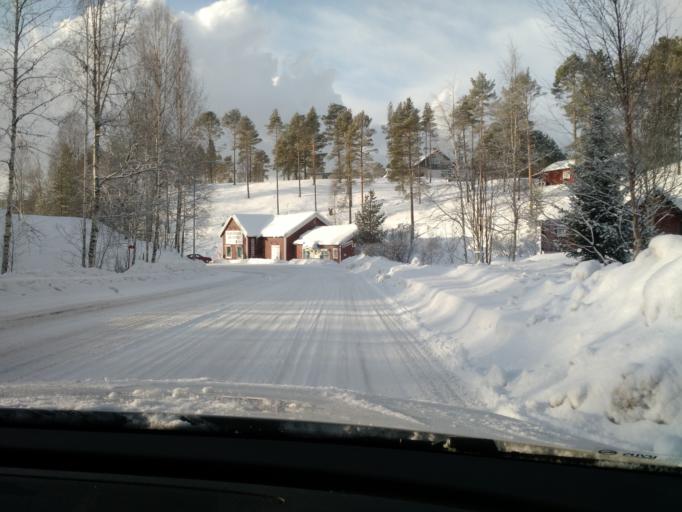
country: NO
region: Hedmark
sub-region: Trysil
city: Innbygda
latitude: 61.8600
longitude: 12.7183
